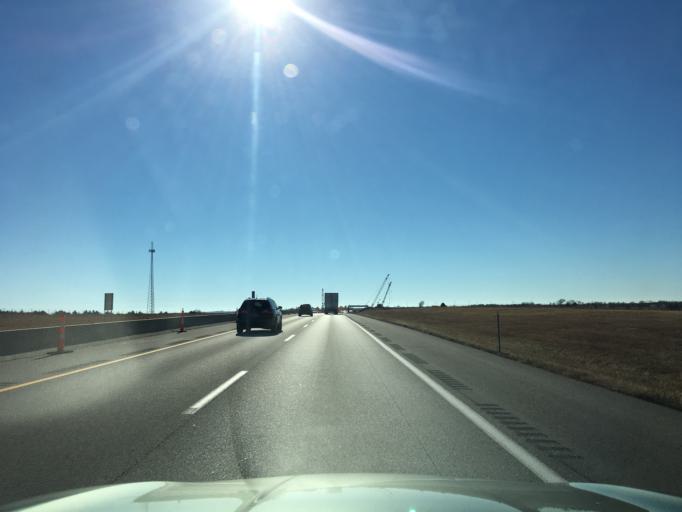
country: US
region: Kansas
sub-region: Sumner County
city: Wellington
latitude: 37.2517
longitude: -97.3390
